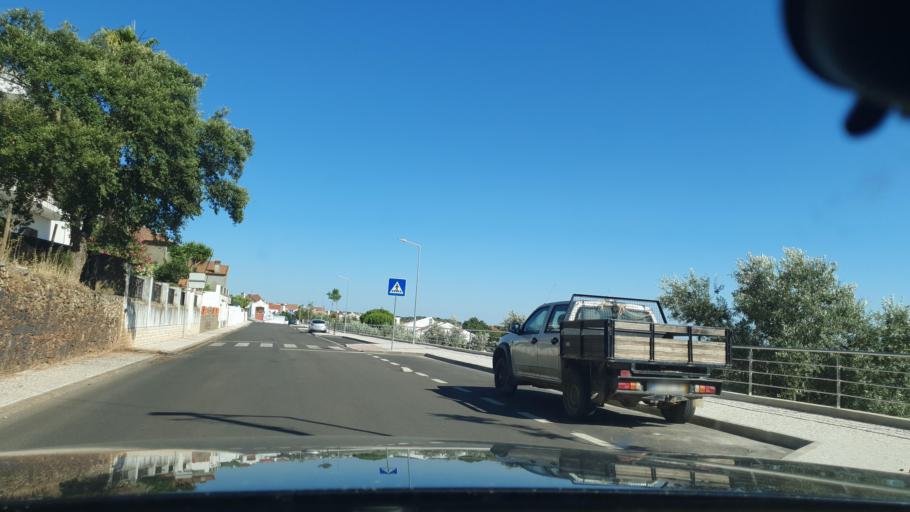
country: PT
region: Evora
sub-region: Alandroal
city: Alandroal
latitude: 38.7053
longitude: -7.4057
